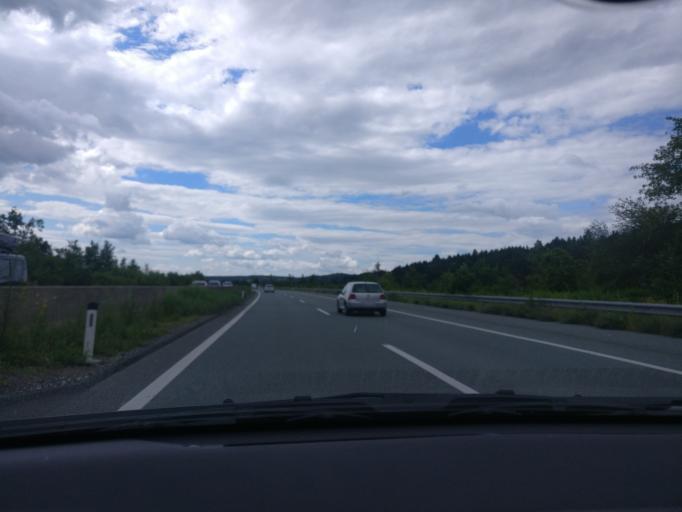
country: AT
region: Styria
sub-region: Politischer Bezirk Hartberg-Fuerstenfeld
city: Sebersdorf
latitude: 47.2014
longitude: 15.9906
